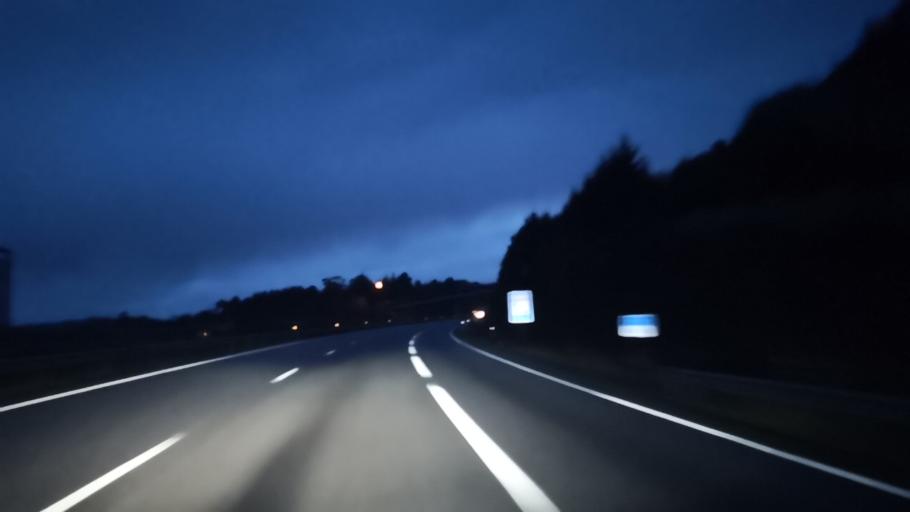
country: PT
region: Braga
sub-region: Guimaraes
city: Brito
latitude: 41.4576
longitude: -8.3575
